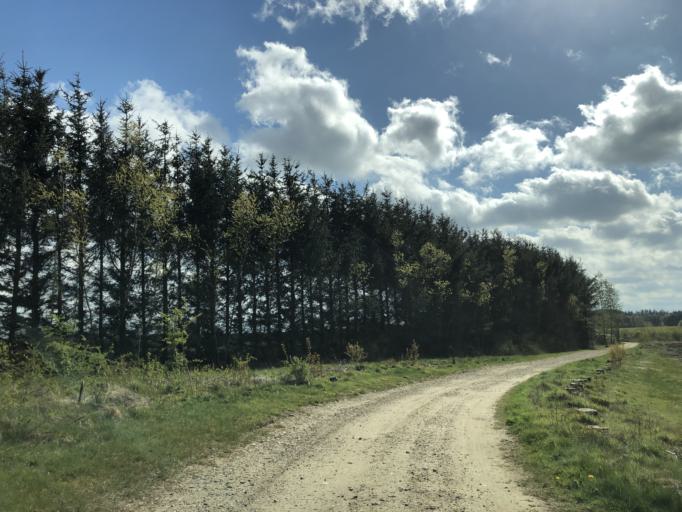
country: DK
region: Central Jutland
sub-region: Herning Kommune
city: Avlum
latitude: 56.2997
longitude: 8.7637
